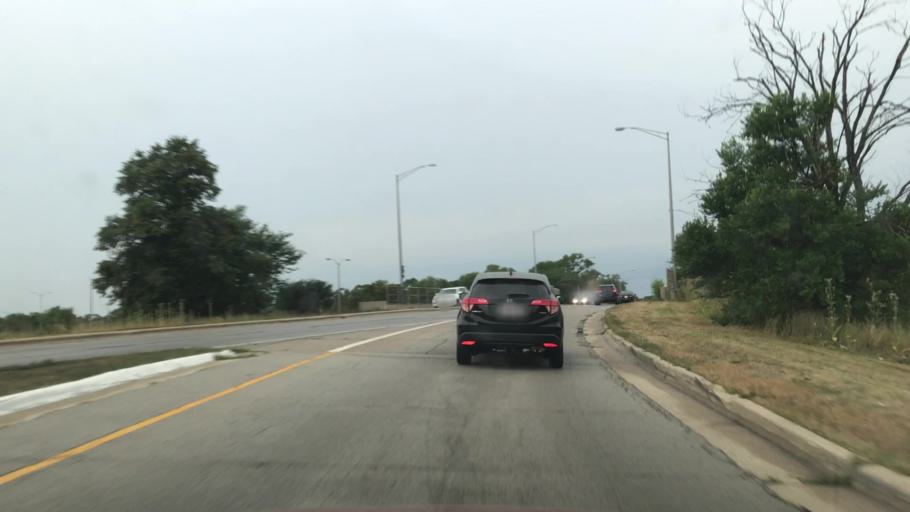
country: US
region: Illinois
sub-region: Cook County
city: Morton Grove
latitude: 42.0410
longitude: -87.7618
